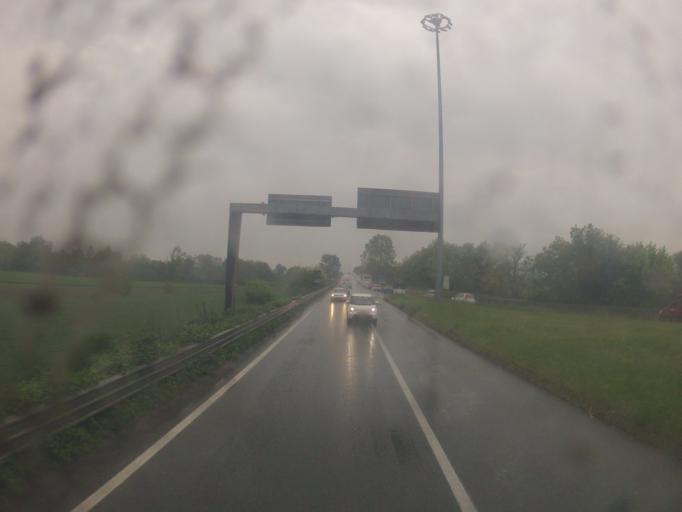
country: IT
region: Piedmont
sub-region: Provincia di Torino
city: Tagliaferro
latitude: 44.9681
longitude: 7.6695
